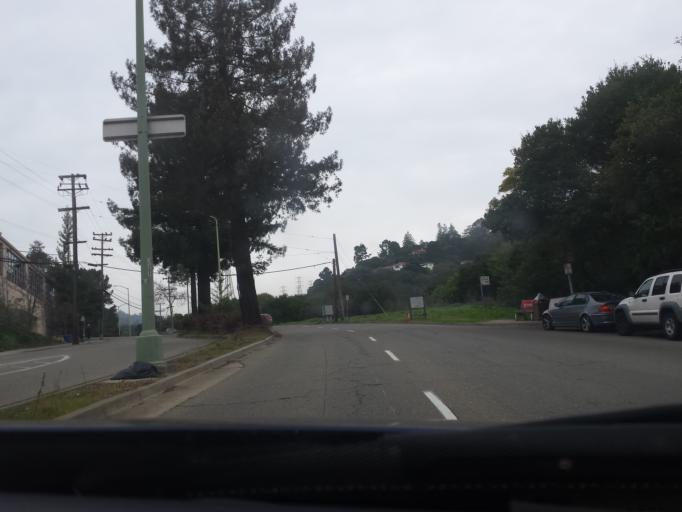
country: US
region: California
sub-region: Alameda County
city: Piedmont
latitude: 37.8129
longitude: -122.2144
